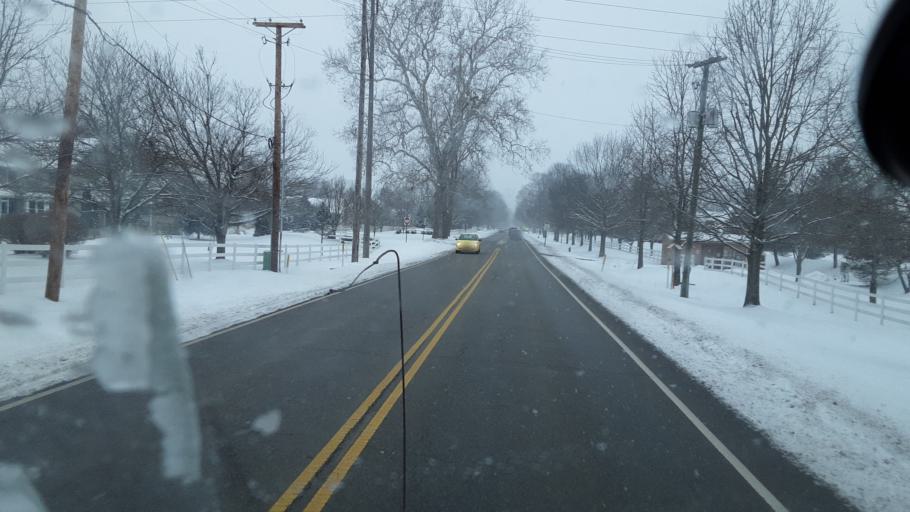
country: US
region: Ohio
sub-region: Licking County
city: Granville
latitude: 40.0610
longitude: -82.4845
